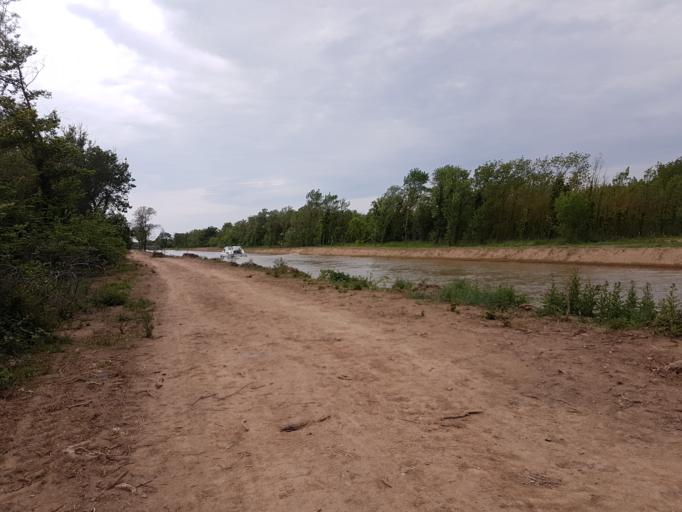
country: FR
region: Languedoc-Roussillon
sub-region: Departement de l'Herault
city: Agde
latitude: 43.3178
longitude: 3.4541
